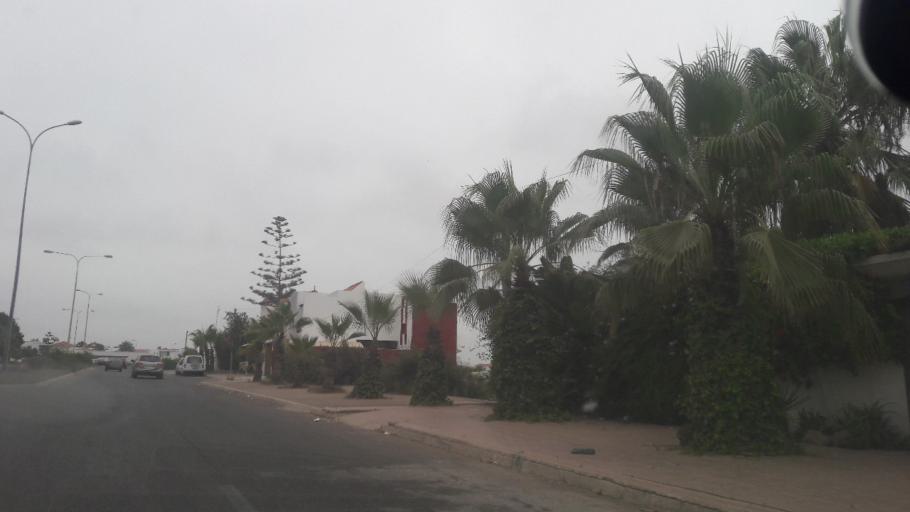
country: MA
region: Souss-Massa-Draa
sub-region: Agadir-Ida-ou-Tnan
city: Agadir
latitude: 30.3910
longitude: -9.5940
